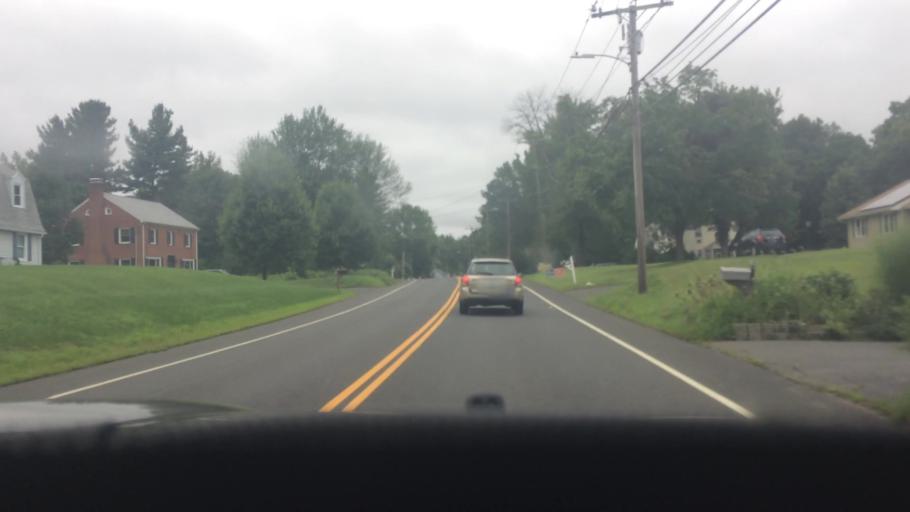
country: US
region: Connecticut
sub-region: Hartford County
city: Blue Hills
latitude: 41.8131
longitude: -72.7354
